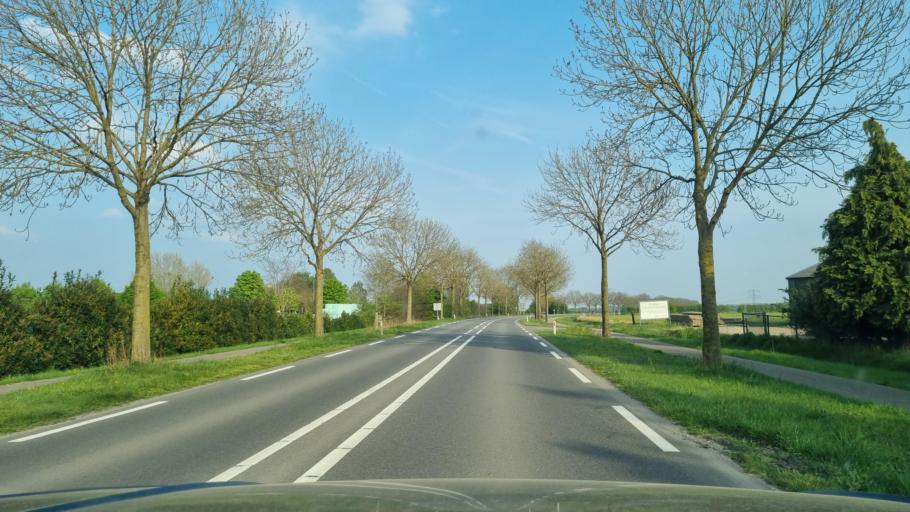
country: NL
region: North Brabant
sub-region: Gemeente Grave
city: Grave
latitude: 51.7415
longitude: 5.7847
